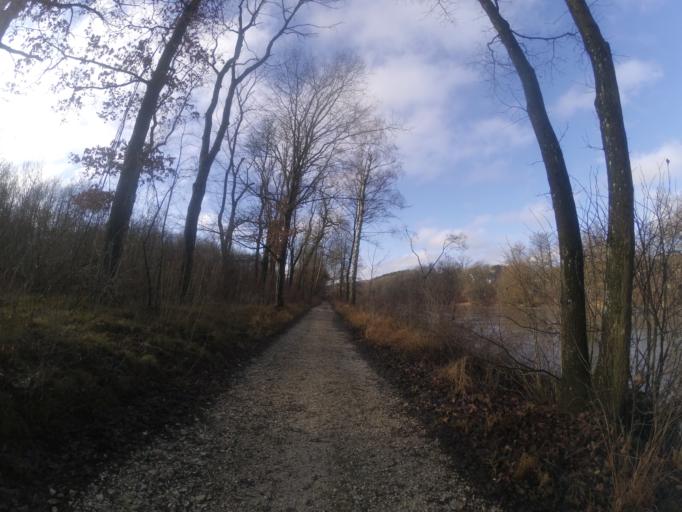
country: DE
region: Bavaria
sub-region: Swabia
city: Neu-Ulm
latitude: 48.4320
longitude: 10.0504
